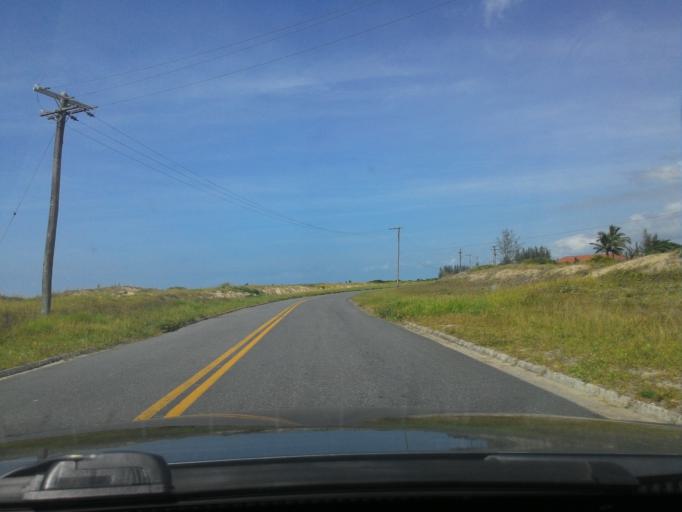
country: BR
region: Sao Paulo
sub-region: Iguape
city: Iguape
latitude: -24.8051
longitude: -47.6356
